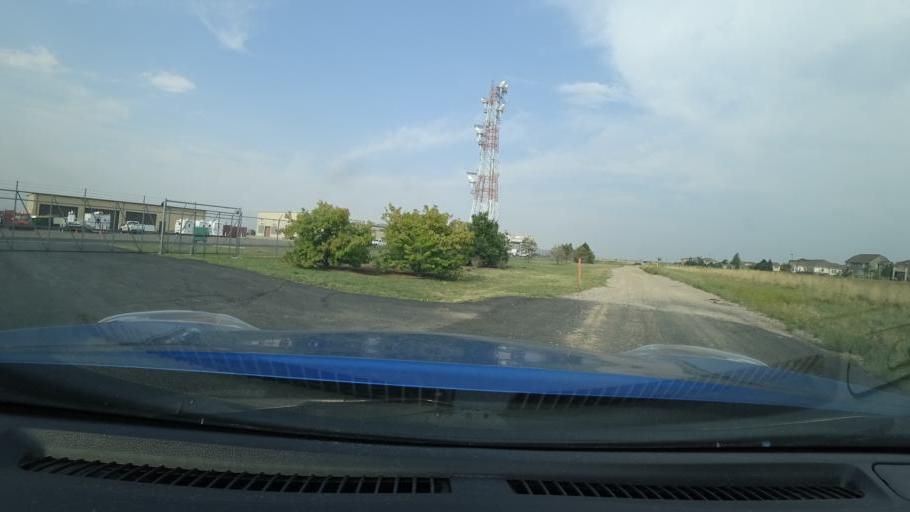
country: US
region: Colorado
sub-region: Adams County
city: Aurora
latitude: 39.7258
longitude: -104.7089
